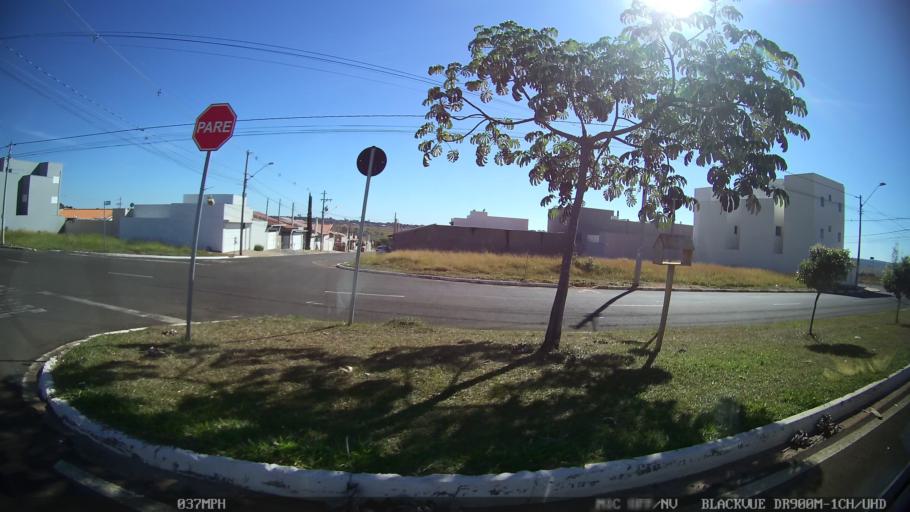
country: BR
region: Sao Paulo
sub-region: Franca
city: Franca
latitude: -20.5646
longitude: -47.3470
